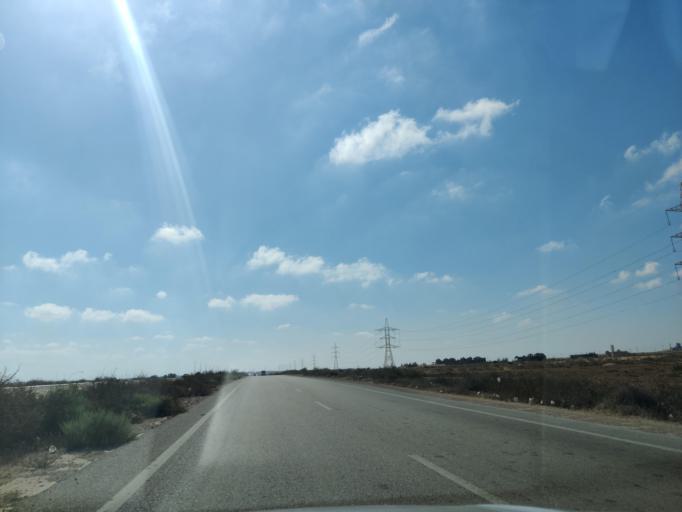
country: EG
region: Muhafazat Matruh
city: Al `Alamayn
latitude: 31.0491
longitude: 28.3317
